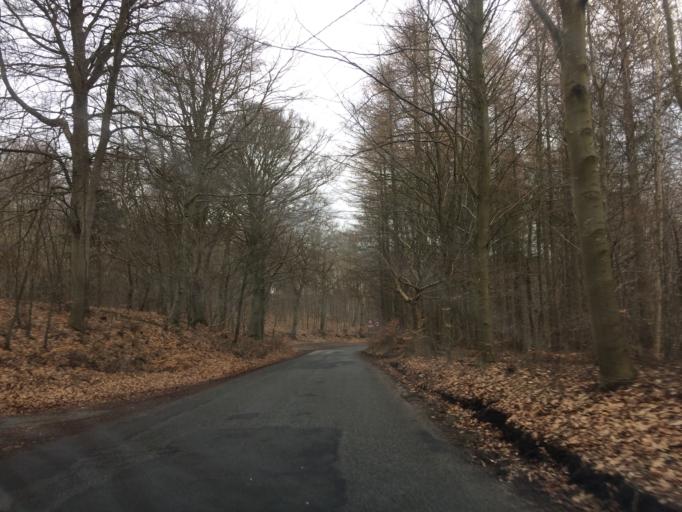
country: DK
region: Central Jutland
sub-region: Arhus Kommune
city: Beder
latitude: 56.1075
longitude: 10.2325
